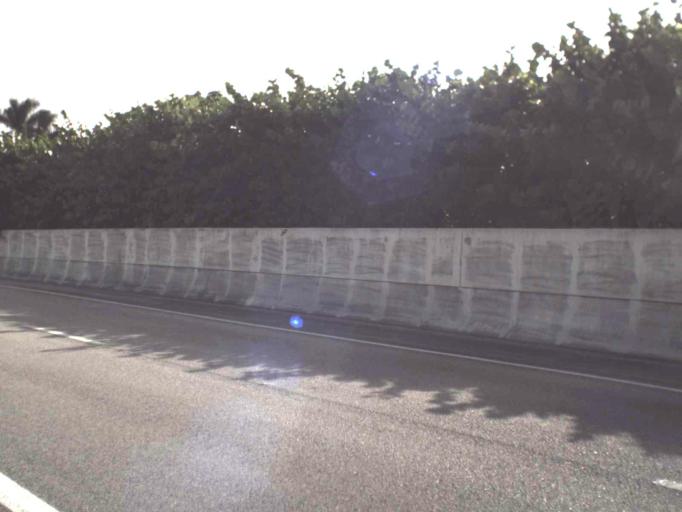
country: US
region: Florida
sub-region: Miami-Dade County
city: Scott Lake
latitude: 25.9523
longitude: -80.2289
